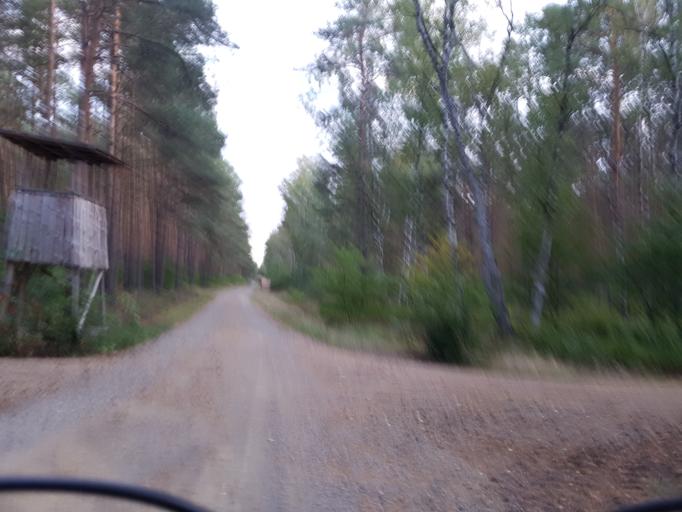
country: DE
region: Brandenburg
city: Schonborn
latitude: 51.5703
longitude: 13.4623
